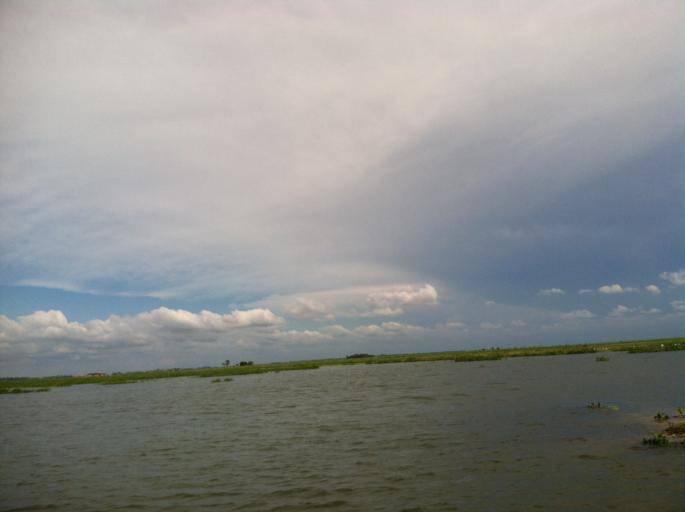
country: BD
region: Sylhet
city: Baniachang
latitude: 24.5716
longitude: 91.3566
